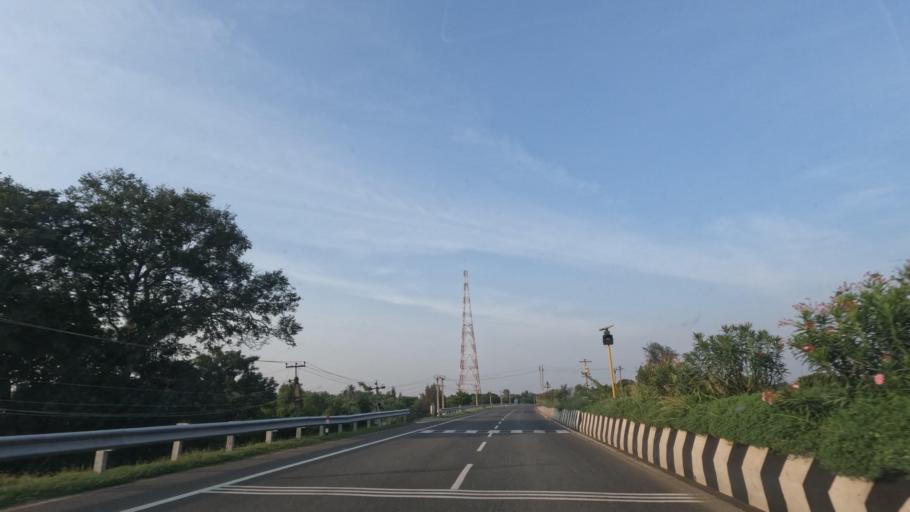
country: IN
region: Tamil Nadu
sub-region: Kancheepuram
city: Mamallapuram
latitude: 12.7081
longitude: 80.2241
